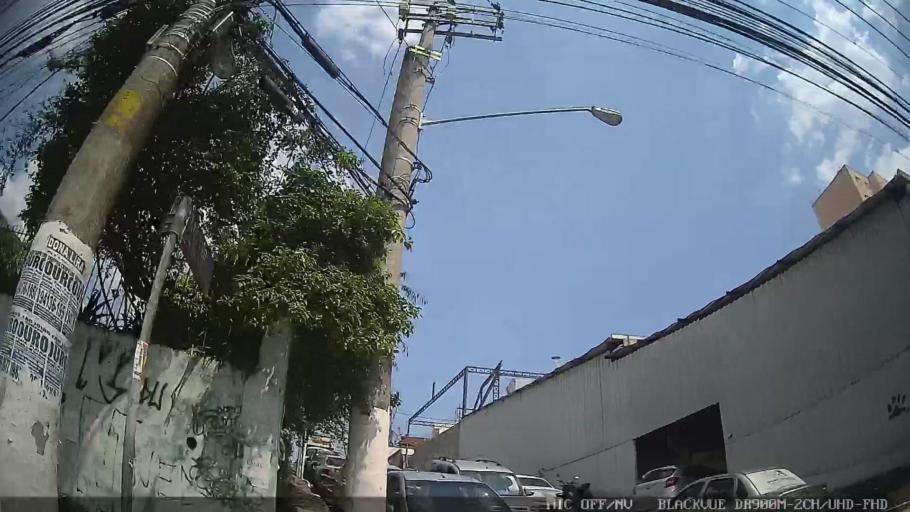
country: BR
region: Sao Paulo
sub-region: Taboao Da Serra
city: Taboao da Serra
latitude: -23.6540
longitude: -46.7597
